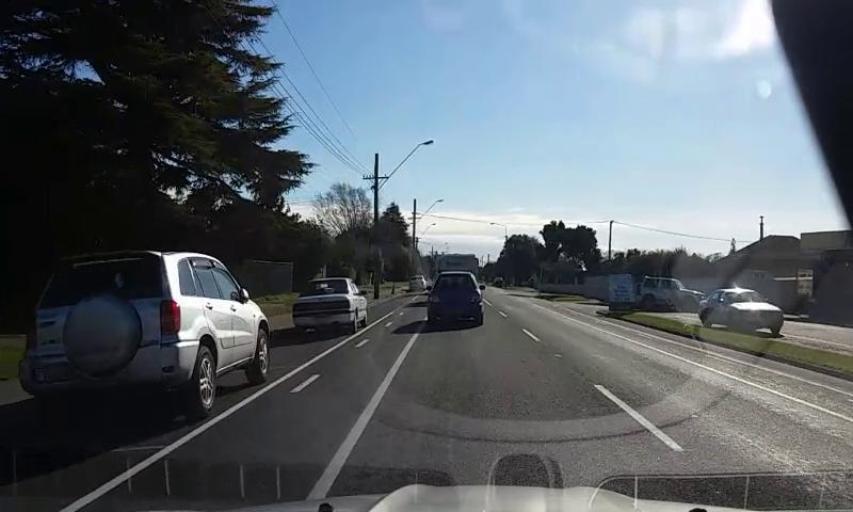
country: NZ
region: Canterbury
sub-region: Christchurch City
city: Christchurch
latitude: -43.4992
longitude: 172.6619
